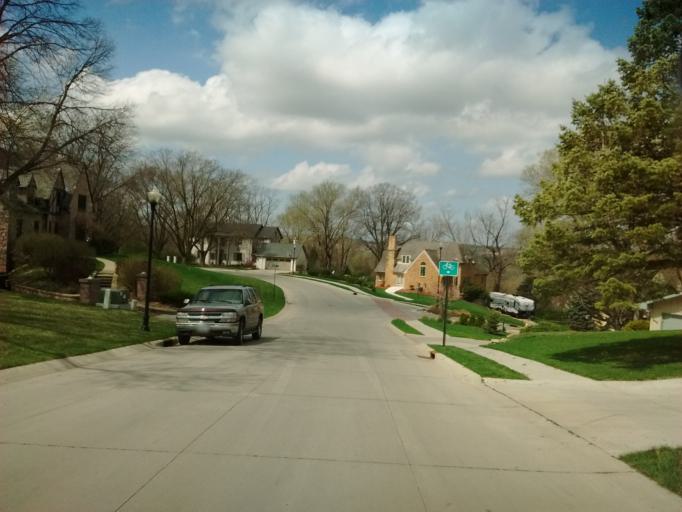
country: US
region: Iowa
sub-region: Woodbury County
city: Sioux City
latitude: 42.5175
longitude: -96.4133
